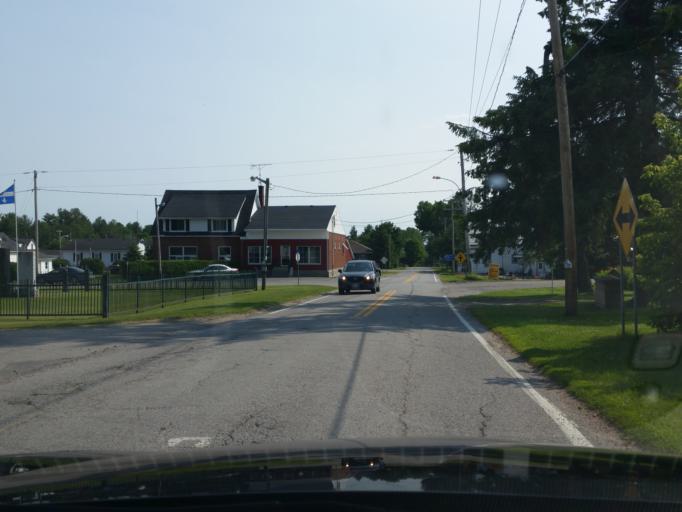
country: CA
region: Quebec
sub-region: Outaouais
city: Shawville
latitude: 45.5316
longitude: -76.4578
